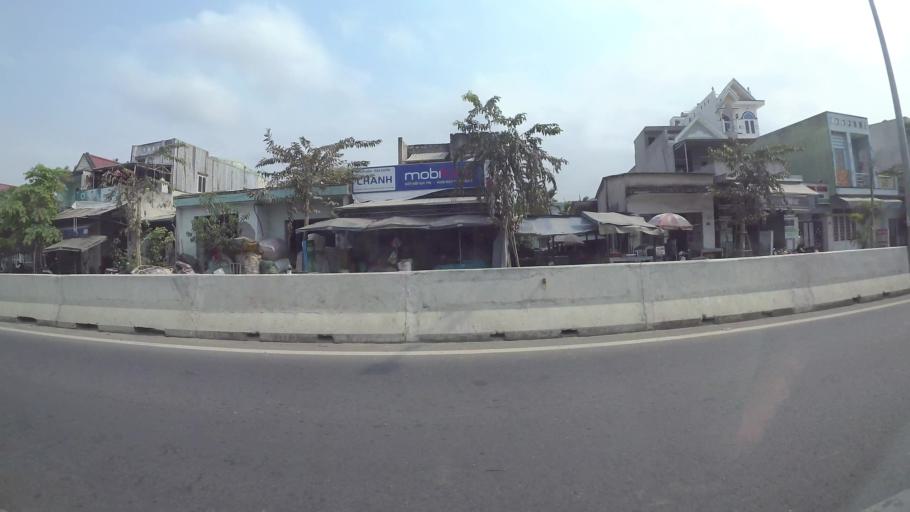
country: VN
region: Da Nang
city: Lien Chieu
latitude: 16.0519
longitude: 108.1520
